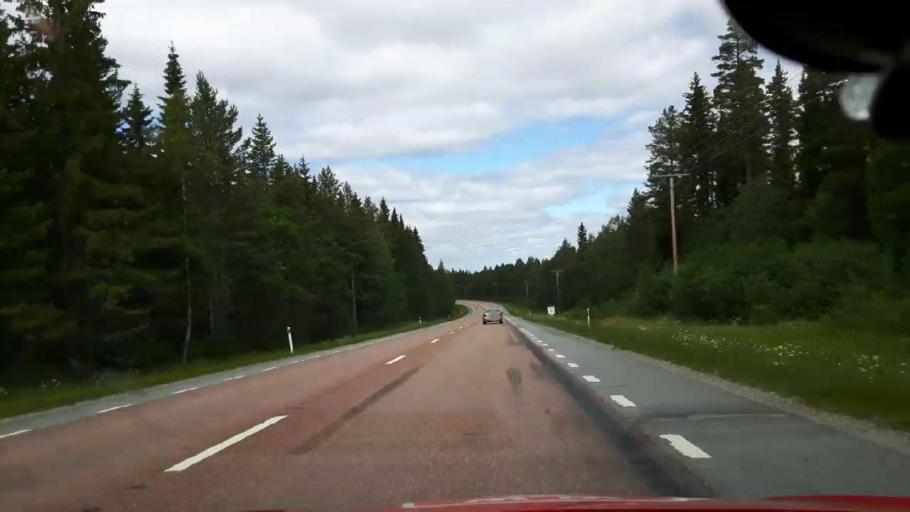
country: SE
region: Jaemtland
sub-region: Braecke Kommun
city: Braecke
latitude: 62.8101
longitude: 15.3651
